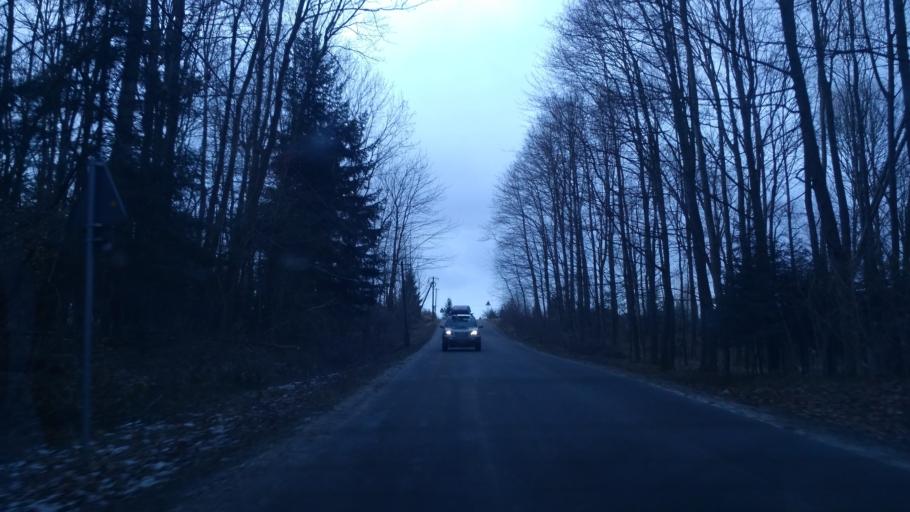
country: PL
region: Subcarpathian Voivodeship
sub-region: Powiat rzeszowski
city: Blazowa
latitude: 49.8518
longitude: 22.0899
